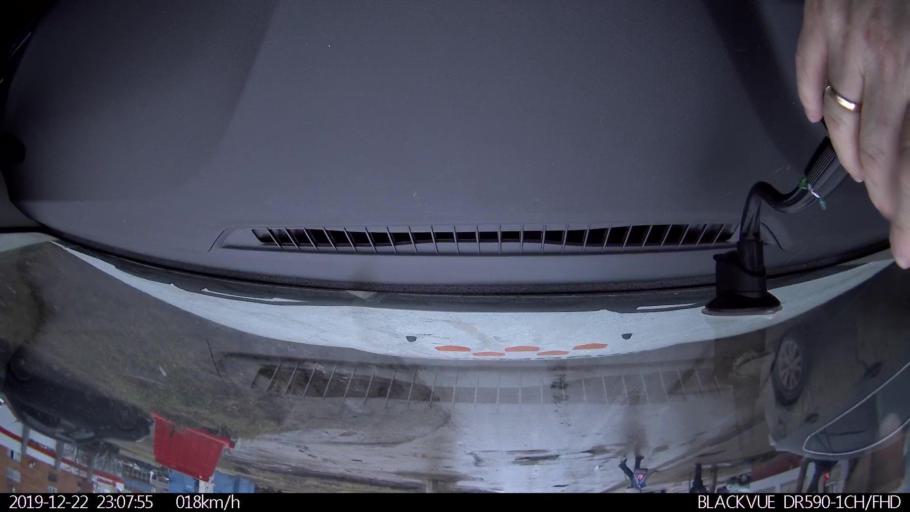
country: RU
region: Nizjnij Novgorod
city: Gorbatovka
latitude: 56.2622
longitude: 43.8585
